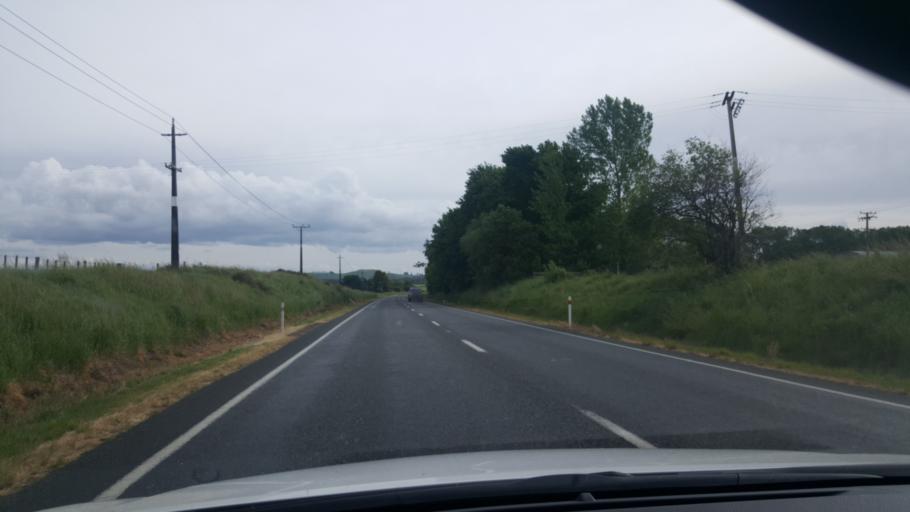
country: NZ
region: Bay of Plenty
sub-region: Rotorua District
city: Rotorua
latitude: -38.3939
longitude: 176.3374
